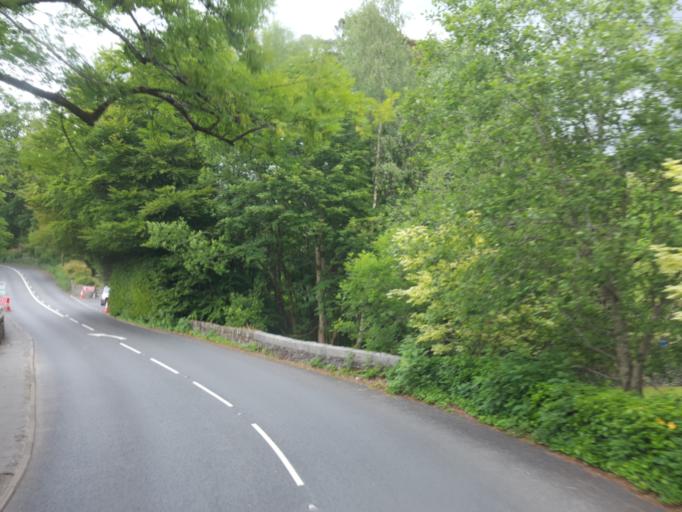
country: GB
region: England
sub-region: Cumbria
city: Ambleside
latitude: 54.4375
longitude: -2.9699
